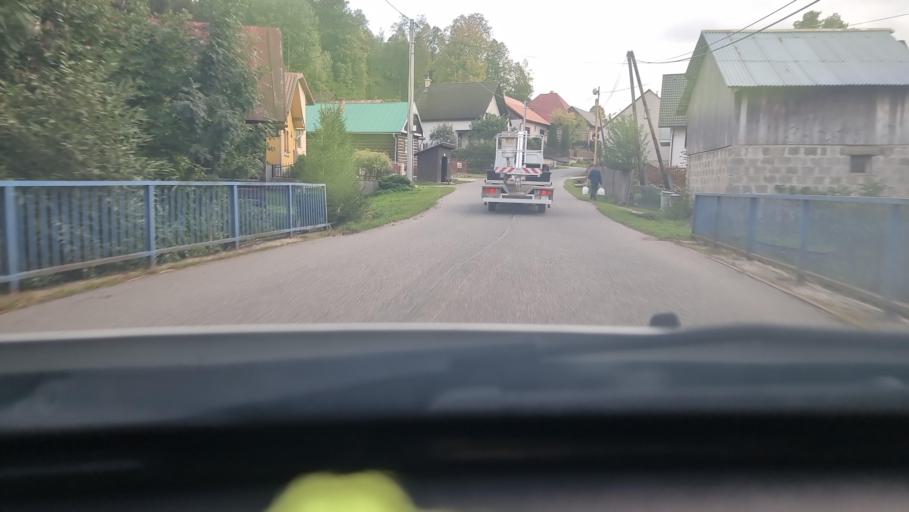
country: PL
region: Lesser Poland Voivodeship
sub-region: Powiat nowotarski
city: Szczawnica
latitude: 49.3351
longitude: 20.4374
